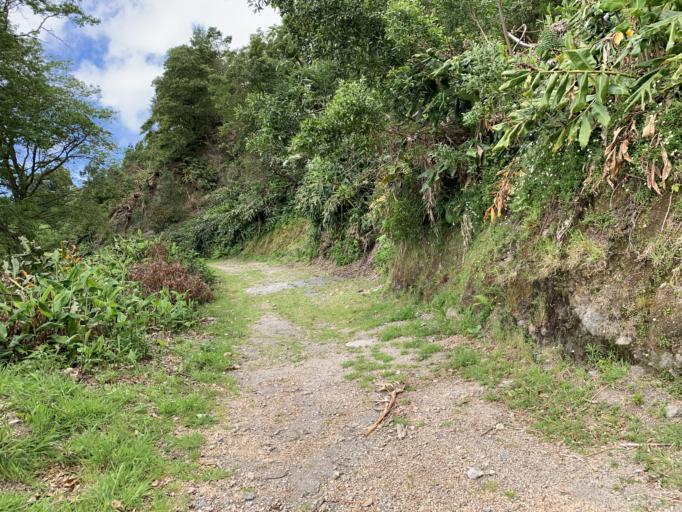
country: PT
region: Azores
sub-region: Ponta Delgada
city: Arrifes
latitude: 37.8476
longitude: -25.7849
